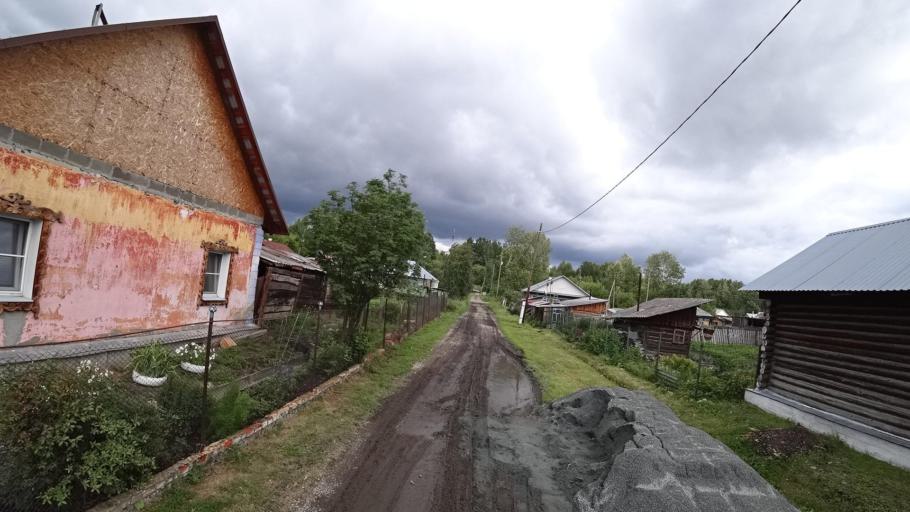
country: RU
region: Sverdlovsk
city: Kamyshlov
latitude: 56.8587
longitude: 62.7175
